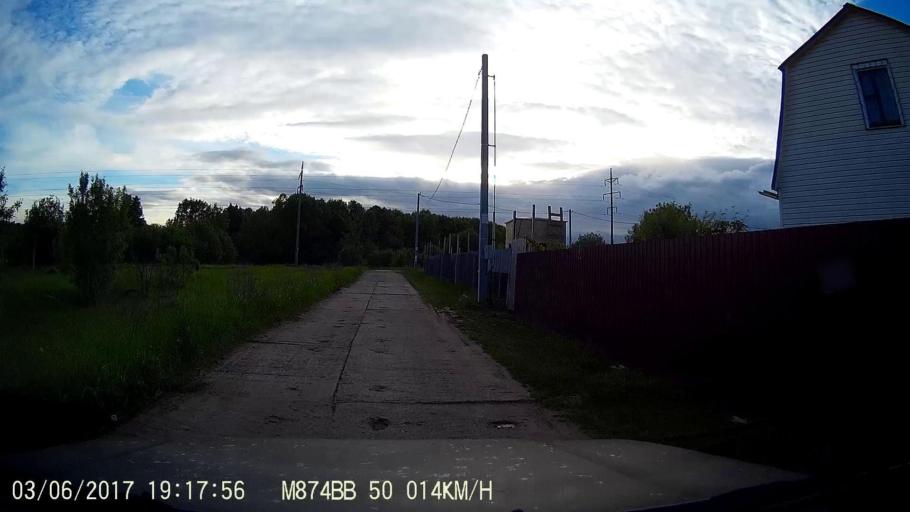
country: RU
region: Moskovskaya
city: Sychevo
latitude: 55.0689
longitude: 38.7364
